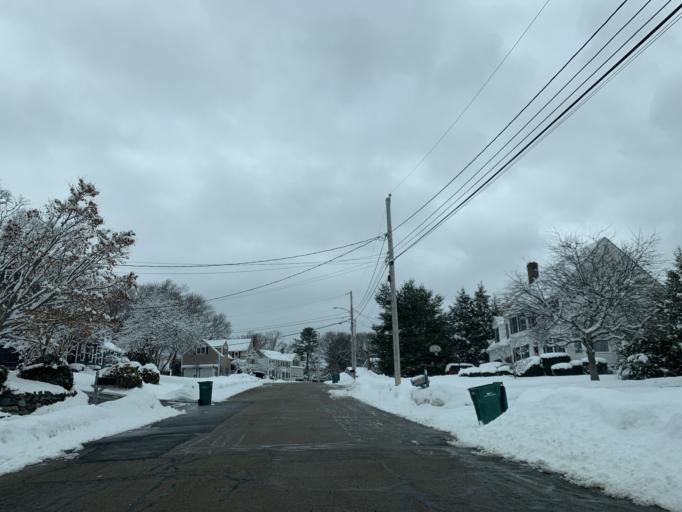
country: US
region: Massachusetts
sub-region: Norfolk County
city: Norwood
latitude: 42.1709
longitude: -71.1761
